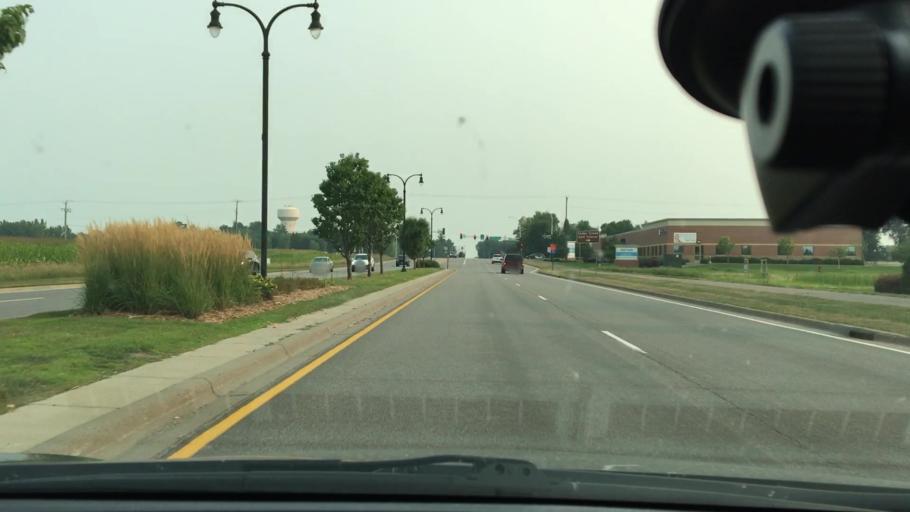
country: US
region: Minnesota
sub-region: Wright County
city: Albertville
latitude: 45.2267
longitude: -93.6645
